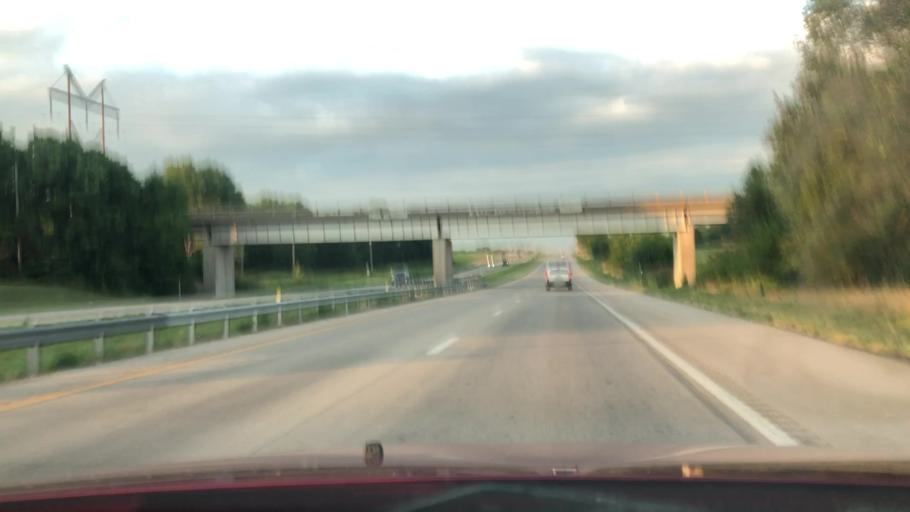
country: US
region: Missouri
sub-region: Greene County
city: Battlefield
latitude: 37.1489
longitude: -93.4229
